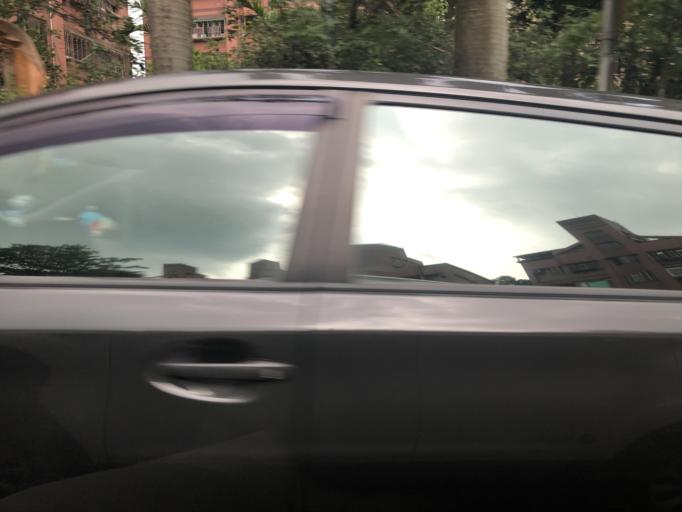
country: TW
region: Taiwan
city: Daxi
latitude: 24.9089
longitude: 121.3583
